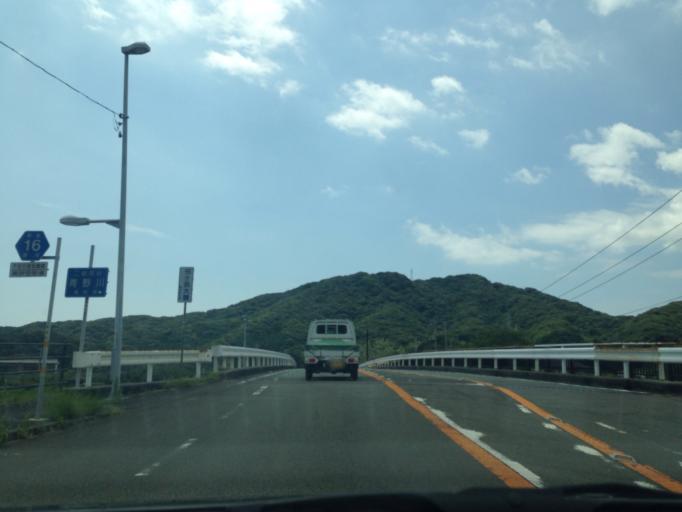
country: JP
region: Shizuoka
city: Shimoda
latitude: 34.6420
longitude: 138.8869
